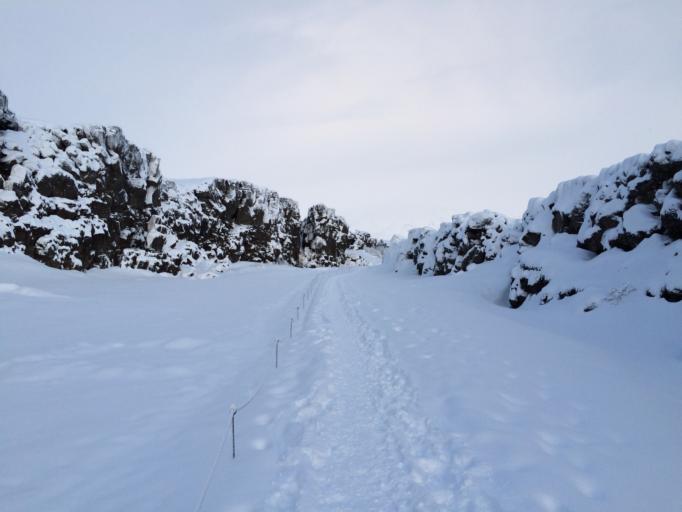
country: IS
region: South
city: Hveragerdi
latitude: 64.2662
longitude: -21.1169
